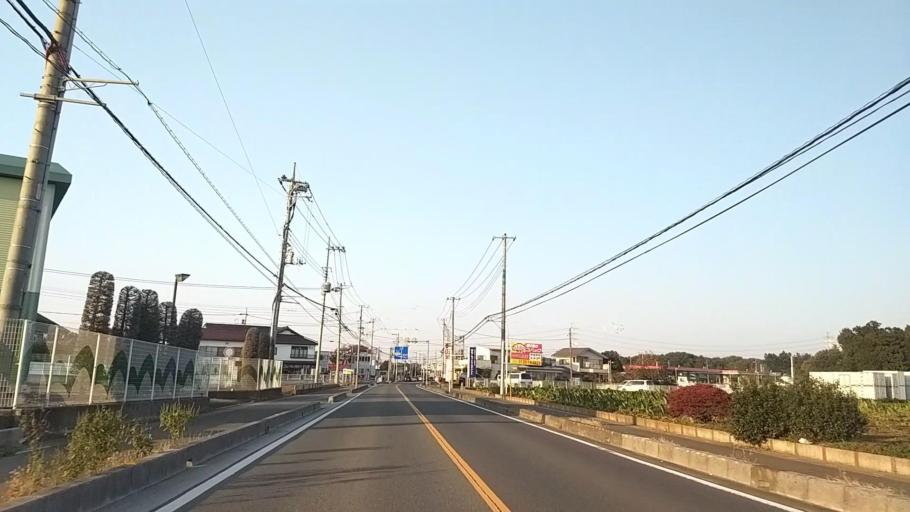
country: JP
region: Saitama
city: Tokorozawa
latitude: 35.8329
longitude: 139.4649
